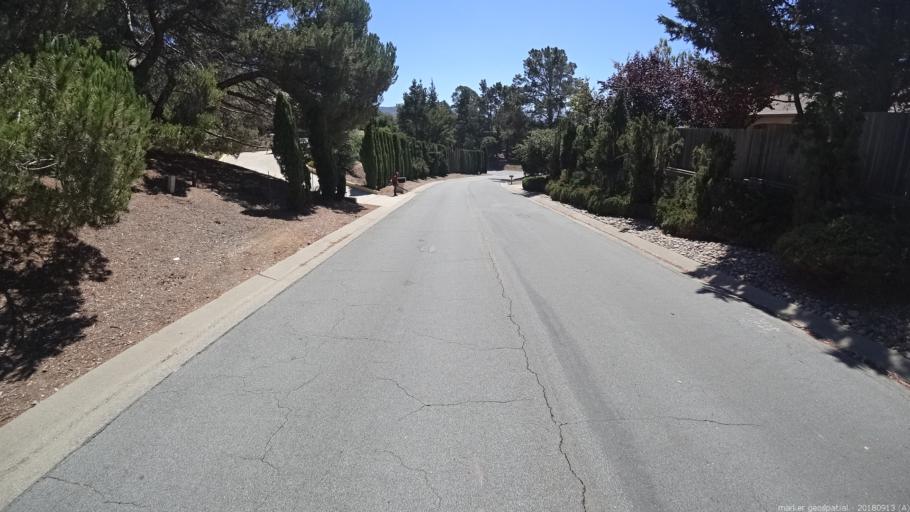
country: US
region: California
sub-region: Monterey County
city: Carmel Valley Village
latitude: 36.5380
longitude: -121.7981
